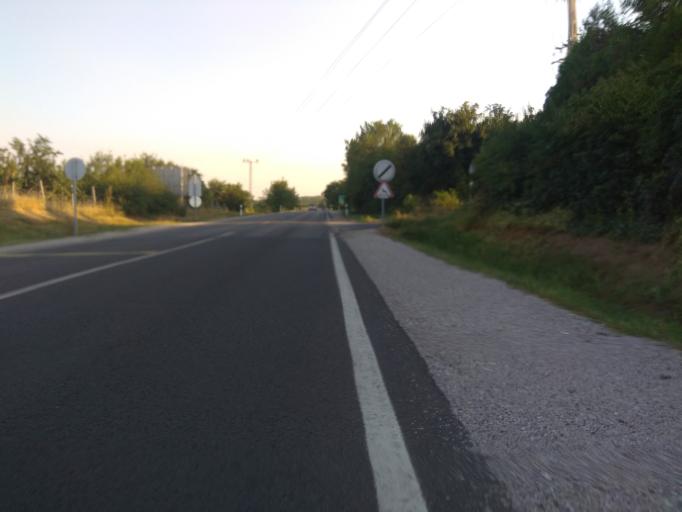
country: HU
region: Borsod-Abauj-Zemplen
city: Nyekladhaza
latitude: 47.9836
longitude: 20.8311
